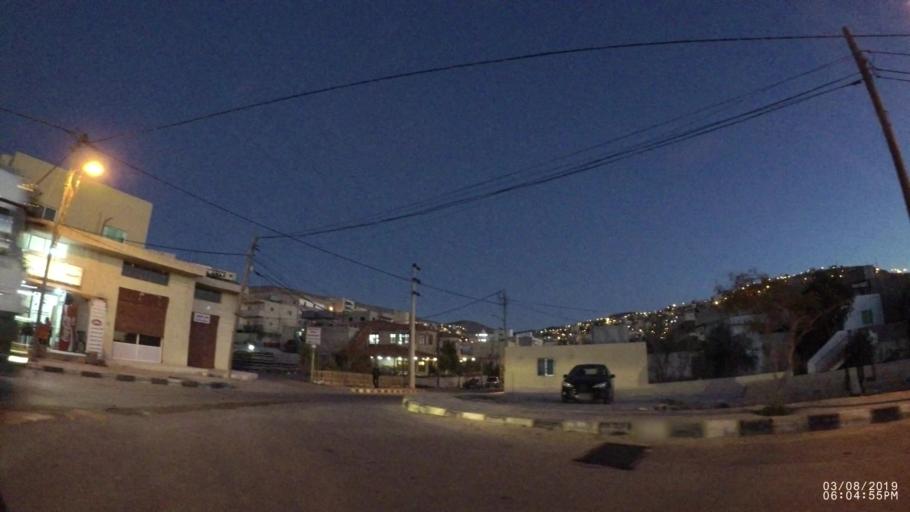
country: JO
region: Ma'an
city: Petra
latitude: 30.3284
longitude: 35.4701
